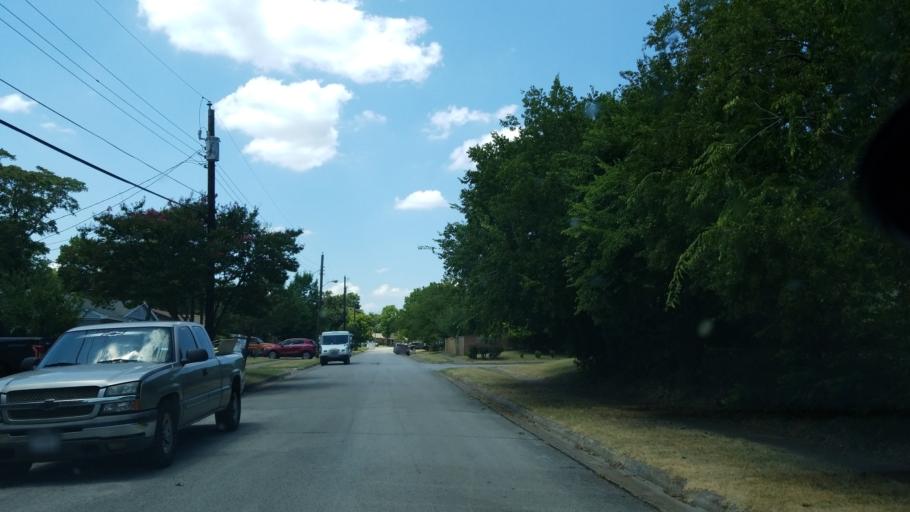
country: US
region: Texas
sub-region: Dallas County
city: Duncanville
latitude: 32.6693
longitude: -96.8980
